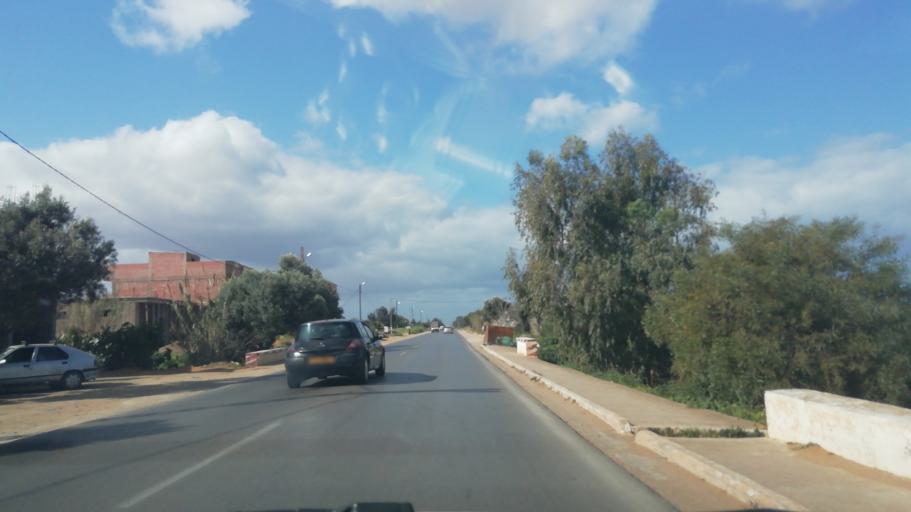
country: DZ
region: Relizane
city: Mazouna
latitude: 36.2582
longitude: 0.5967
